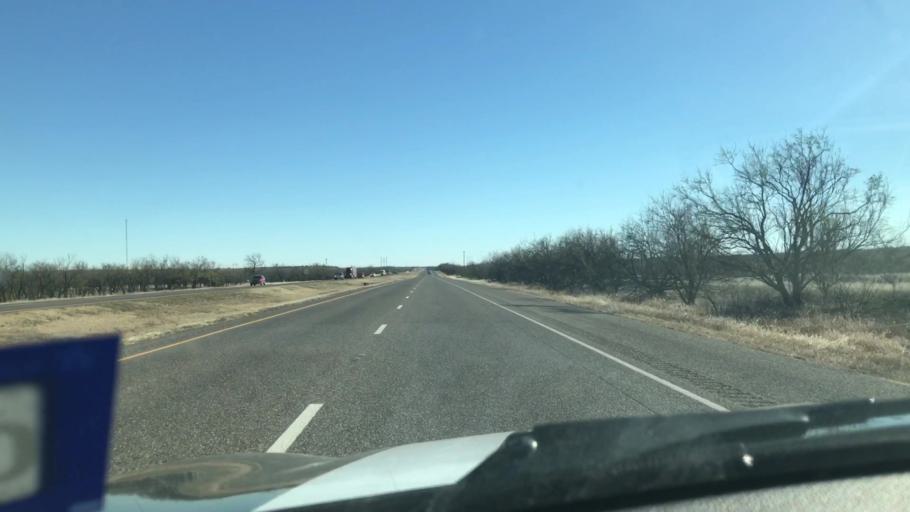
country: US
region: Texas
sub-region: Scurry County
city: Snyder
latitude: 32.8284
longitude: -100.9840
